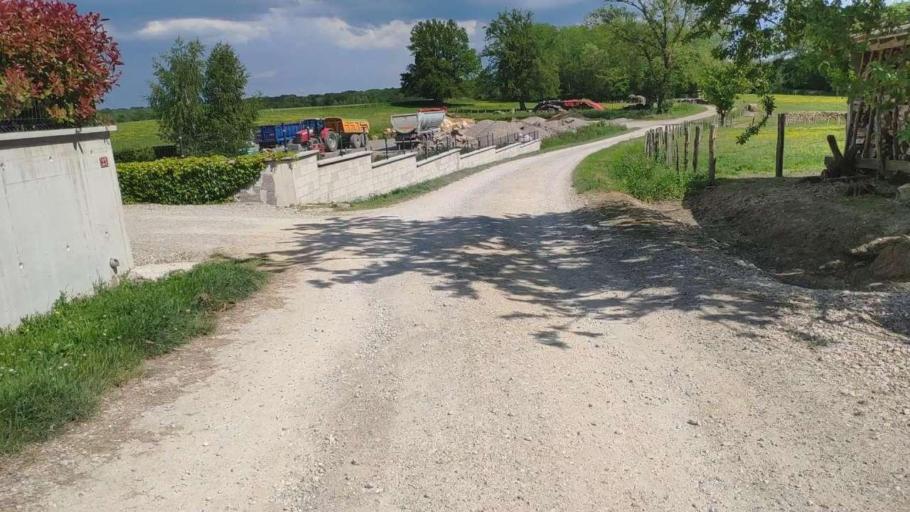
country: FR
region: Franche-Comte
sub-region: Departement du Jura
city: Bletterans
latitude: 46.8262
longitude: 5.4082
